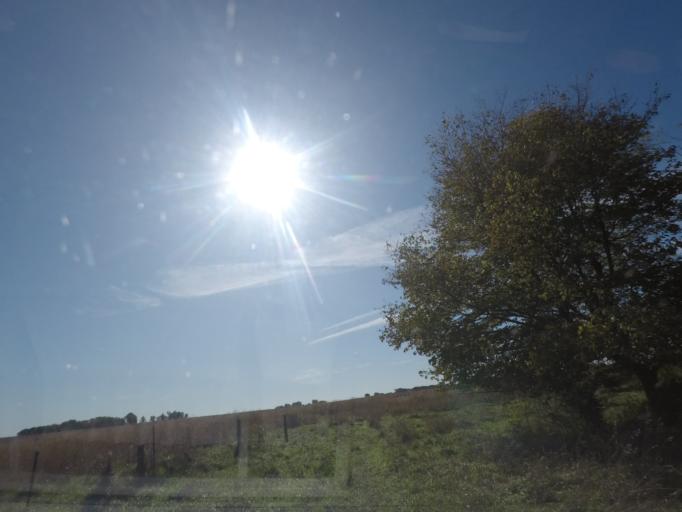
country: US
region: Iowa
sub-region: Story County
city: Nevada
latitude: 42.0334
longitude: -93.3722
